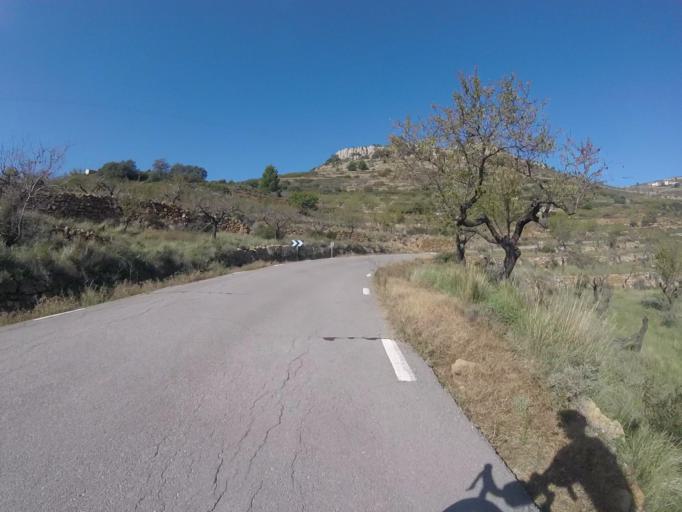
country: ES
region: Valencia
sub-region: Provincia de Castello
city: Sarratella
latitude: 40.2890
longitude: 0.0334
